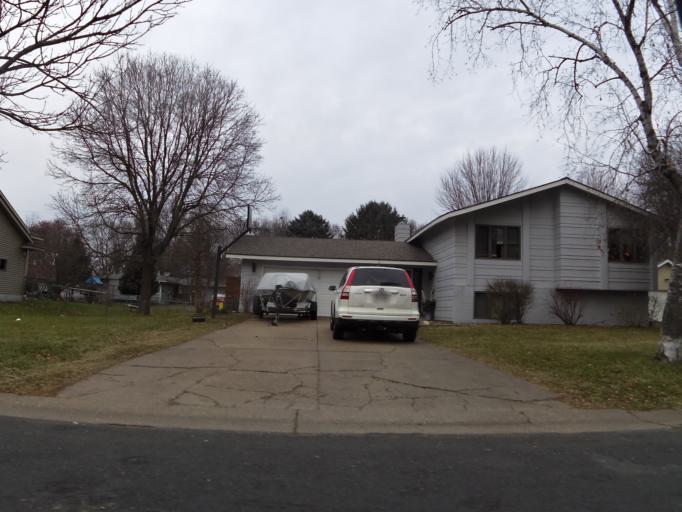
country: US
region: Wisconsin
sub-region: Pierce County
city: River Falls
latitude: 44.8567
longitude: -92.6127
